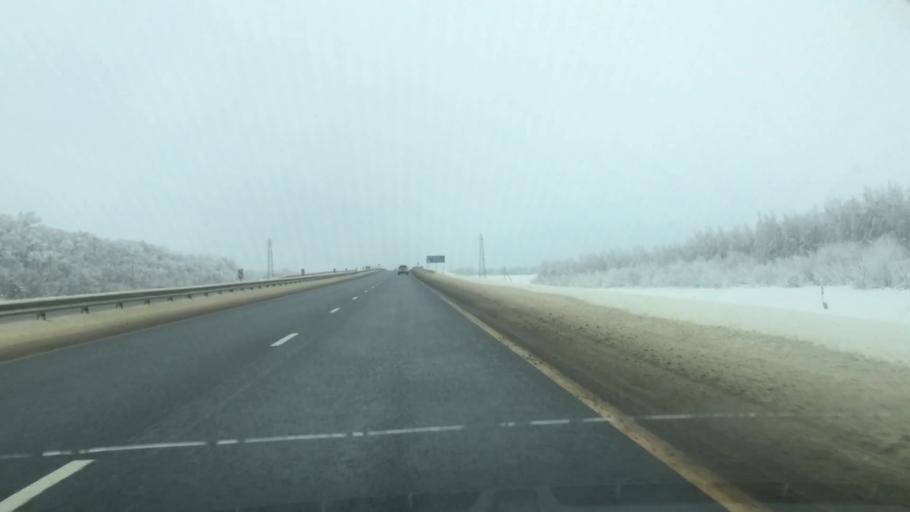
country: RU
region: Lipetsk
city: Zadonsk
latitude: 52.5087
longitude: 38.7557
